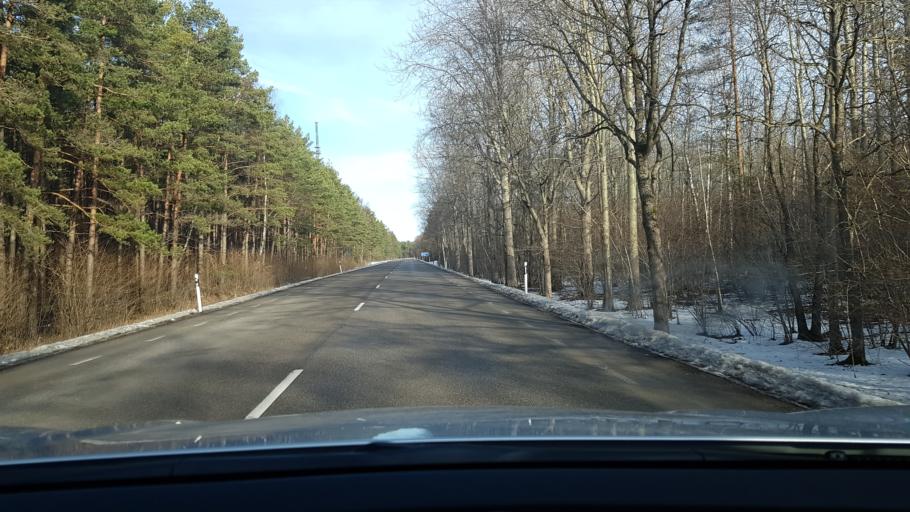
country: EE
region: Saare
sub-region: Orissaare vald
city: Orissaare
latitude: 58.5504
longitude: 23.0610
